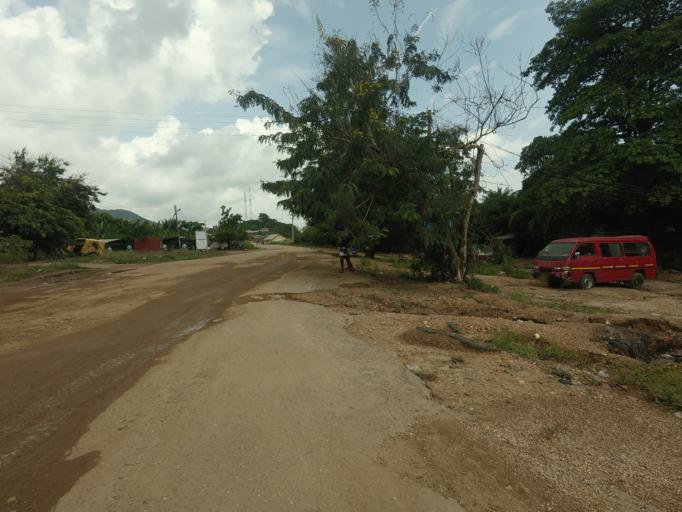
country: GH
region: Volta
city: Ho
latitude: 6.6917
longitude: 0.3347
